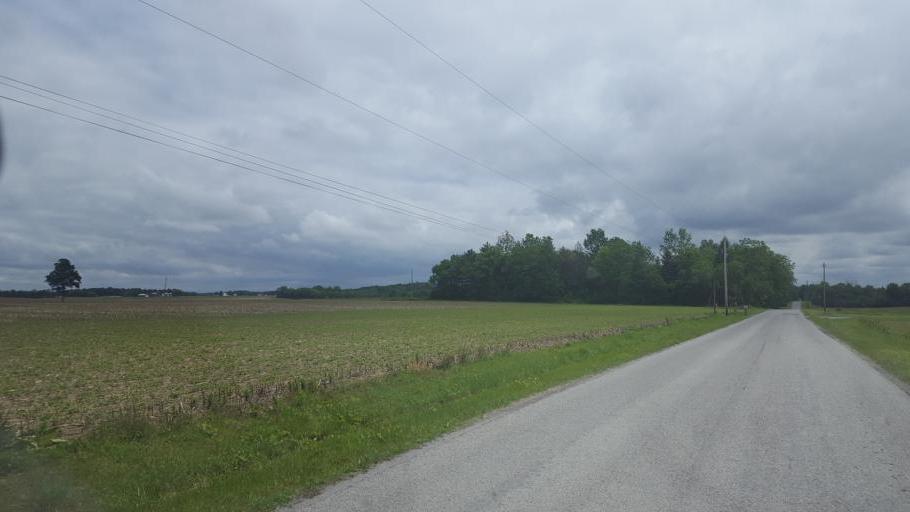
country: US
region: Ohio
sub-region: Crawford County
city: Bucyrus
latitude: 40.7755
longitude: -83.0757
